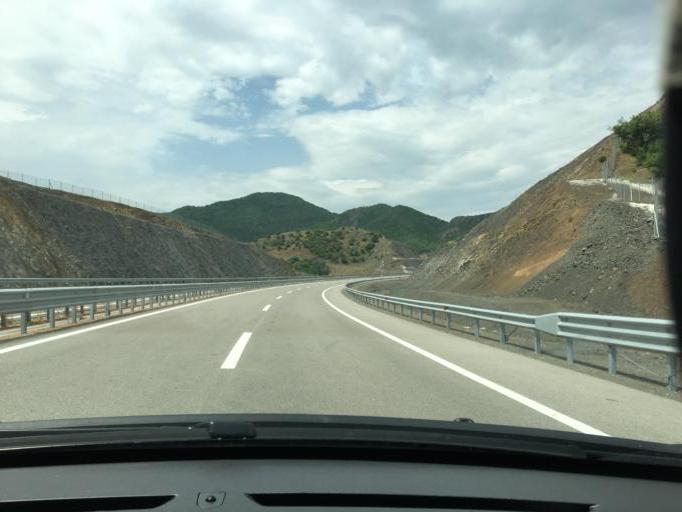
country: MK
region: Demir Kapija
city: Demir Kapija
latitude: 41.3709
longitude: 22.3346
